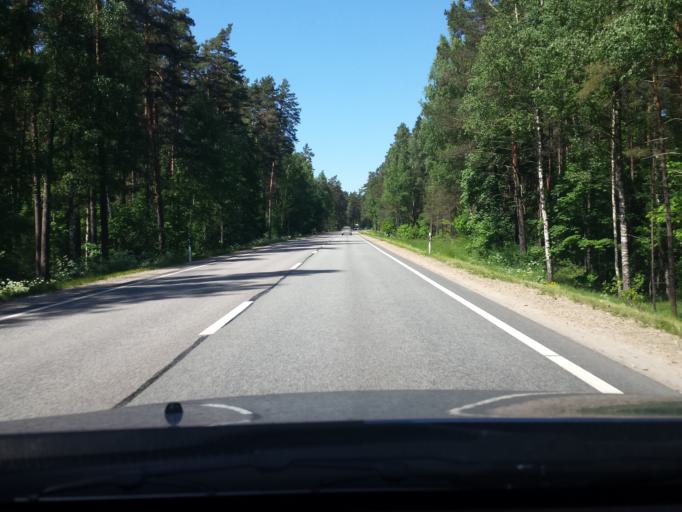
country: LV
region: Riga
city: Bergi
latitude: 56.9907
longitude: 24.3149
